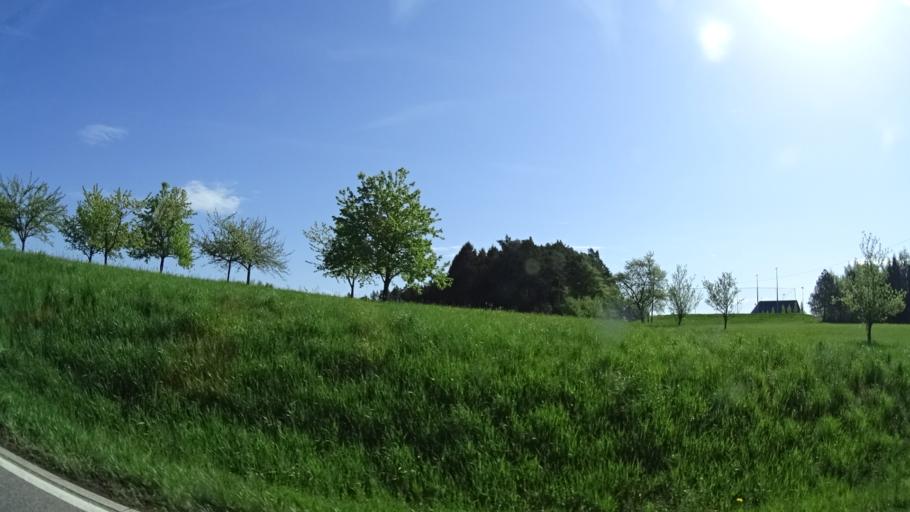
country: DE
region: Baden-Wuerttemberg
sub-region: Karlsruhe Region
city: Ebhausen
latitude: 48.6122
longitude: 8.6542
